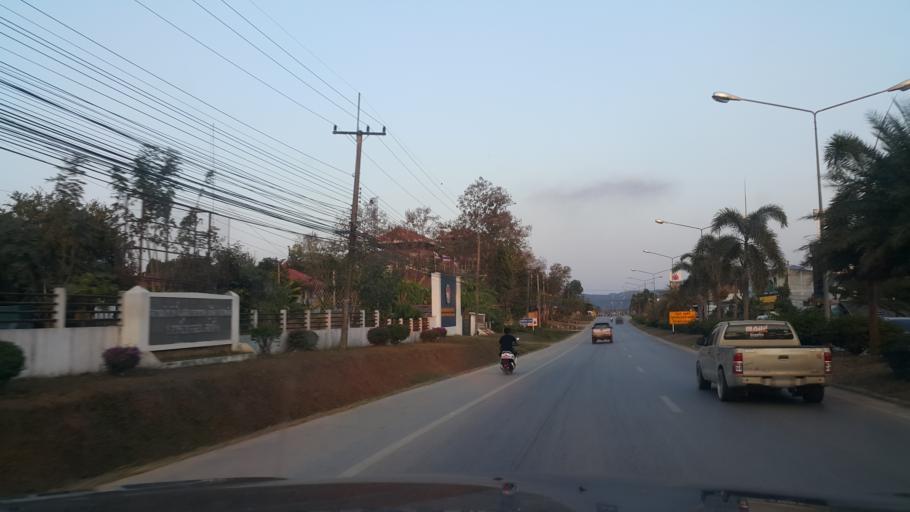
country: TH
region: Loei
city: Loei
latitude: 17.4935
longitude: 101.7075
